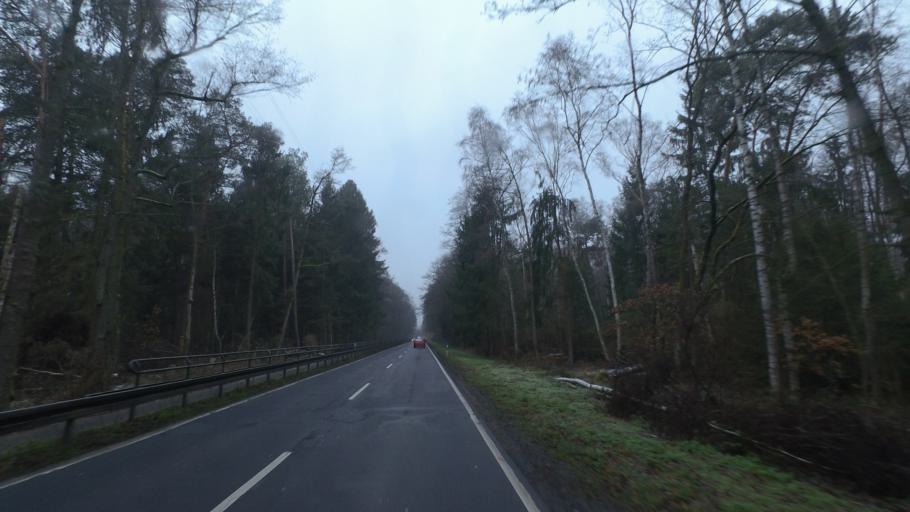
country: DE
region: Hesse
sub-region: Regierungsbezirk Darmstadt
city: Rodgau
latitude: 50.0698
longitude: 8.8989
